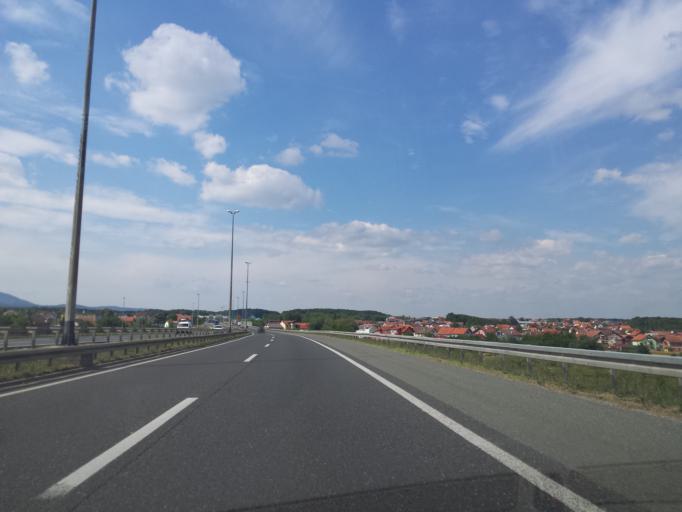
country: HR
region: Grad Zagreb
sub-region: Sesvete
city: Sesvete
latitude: 45.8193
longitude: 16.1383
